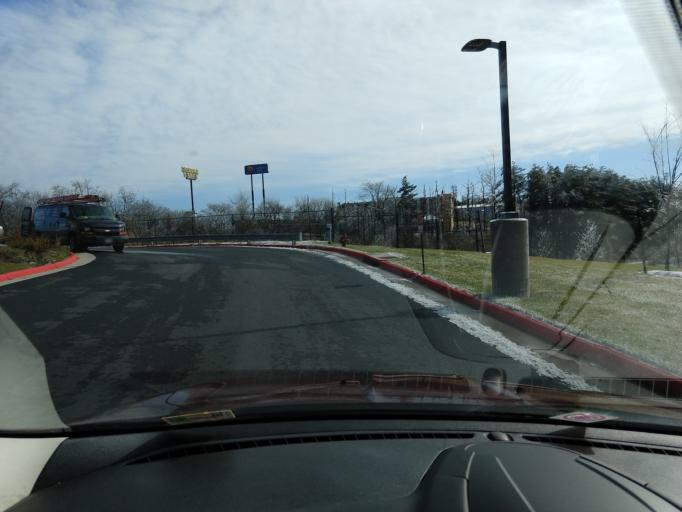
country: US
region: Virginia
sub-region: City of Staunton
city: Staunton
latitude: 38.1305
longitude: -79.0412
